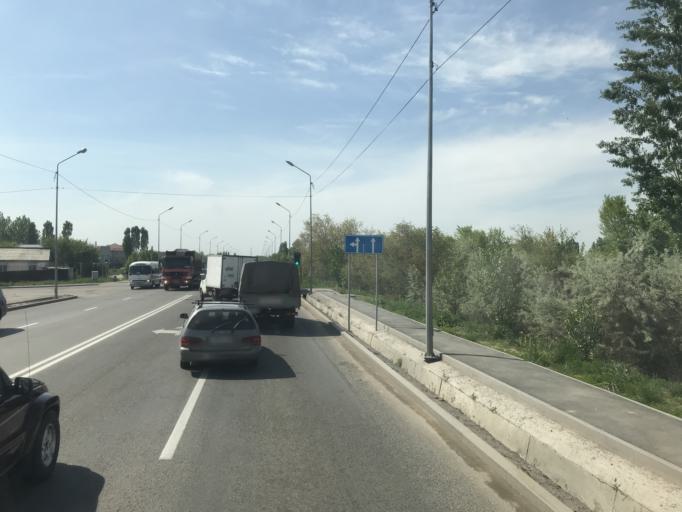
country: KZ
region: Almaty Oblysy
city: Burunday
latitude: 43.3079
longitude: 76.8762
